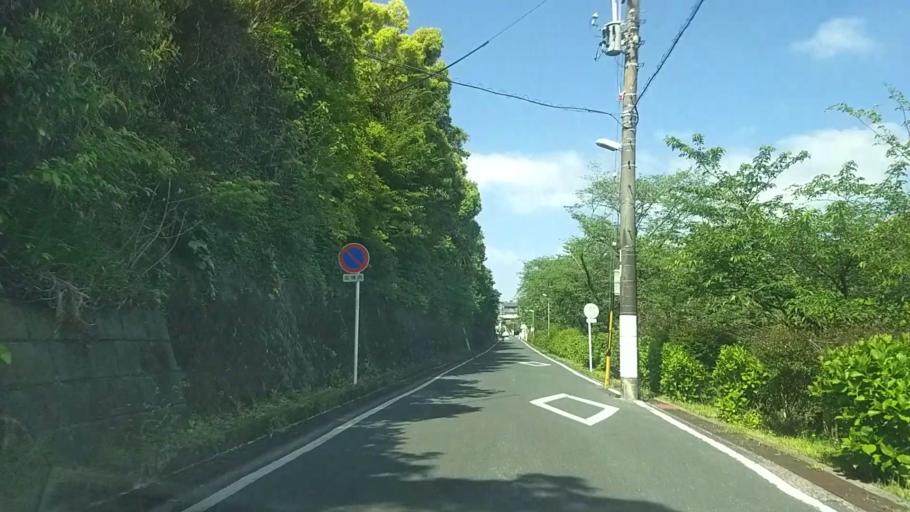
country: JP
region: Shizuoka
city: Hamamatsu
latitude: 34.7140
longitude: 137.7248
